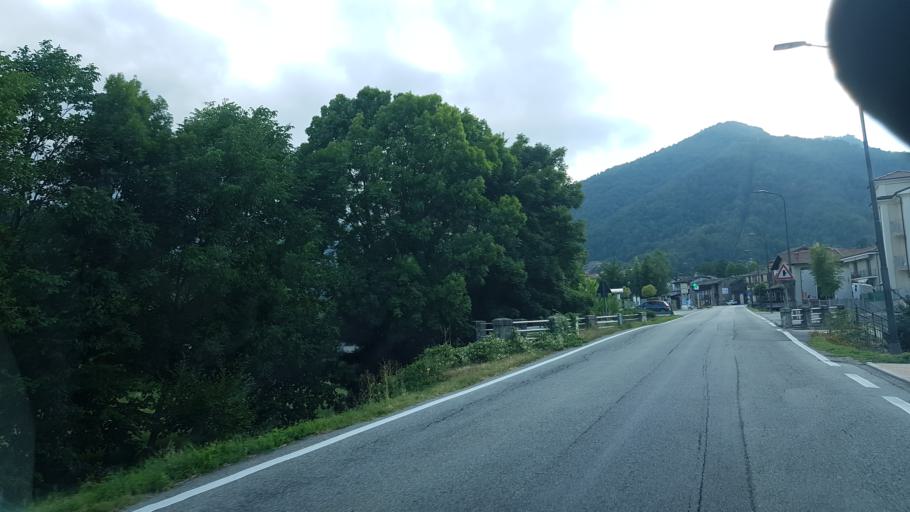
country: IT
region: Piedmont
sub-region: Provincia di Cuneo
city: Brossasco
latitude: 44.5691
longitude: 7.3626
